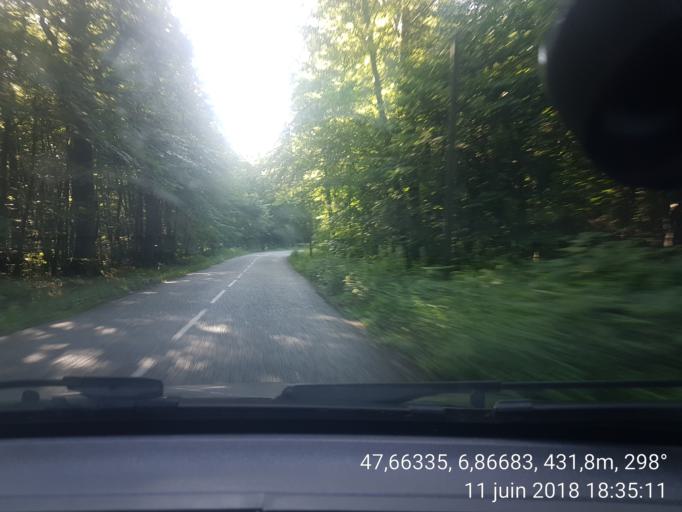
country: FR
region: Franche-Comte
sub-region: Territoire de Belfort
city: Offemont
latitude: 47.6633
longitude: 6.8669
